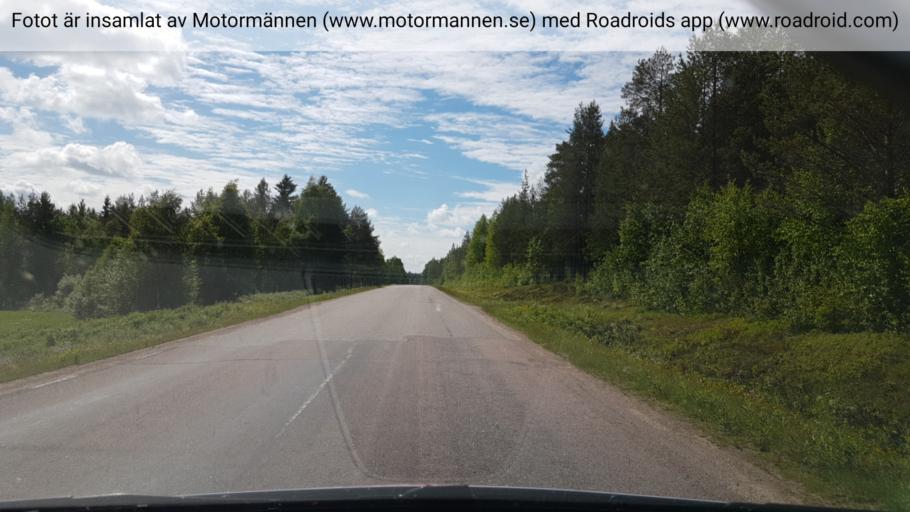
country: FI
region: Lapland
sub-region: Torniolaakso
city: Pello
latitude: 66.5950
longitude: 23.8571
